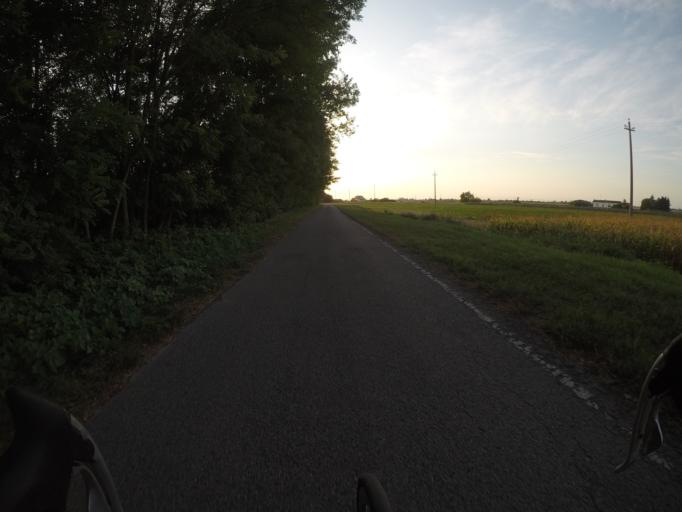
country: IT
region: Veneto
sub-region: Provincia di Rovigo
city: Pincara
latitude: 45.0027
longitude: 11.6381
